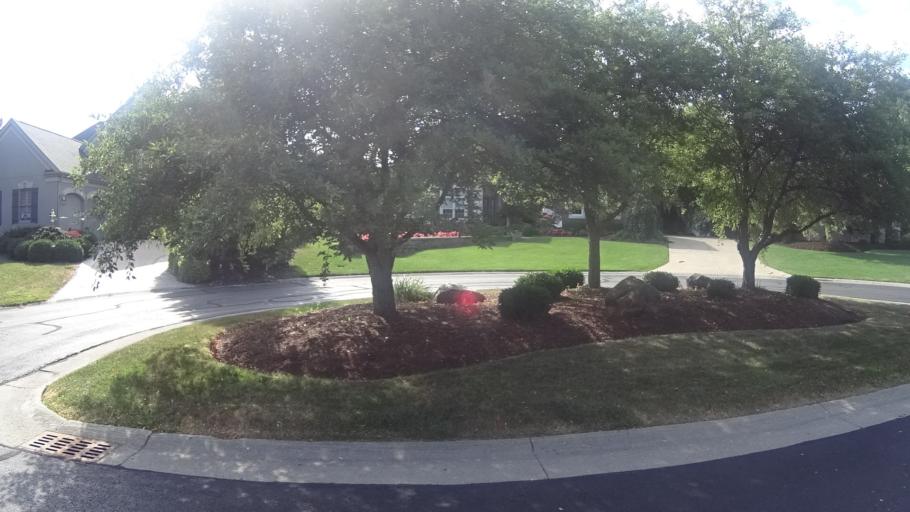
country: US
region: Ohio
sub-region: Erie County
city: Sandusky
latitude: 41.4143
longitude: -82.6624
